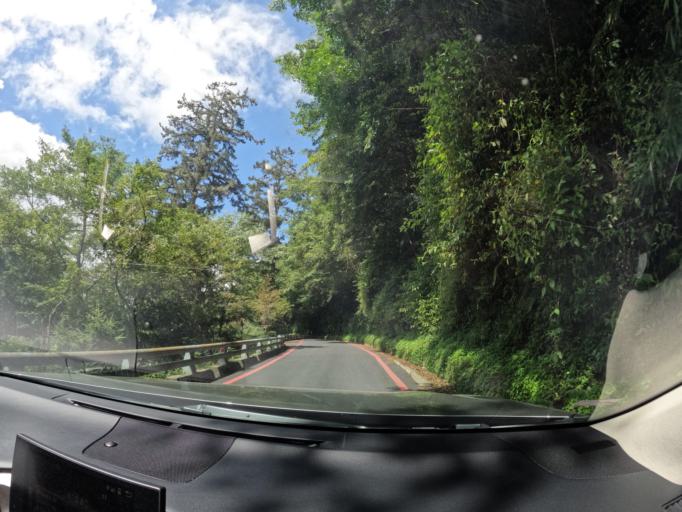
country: TW
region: Taiwan
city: Yujing
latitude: 23.2603
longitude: 120.9216
